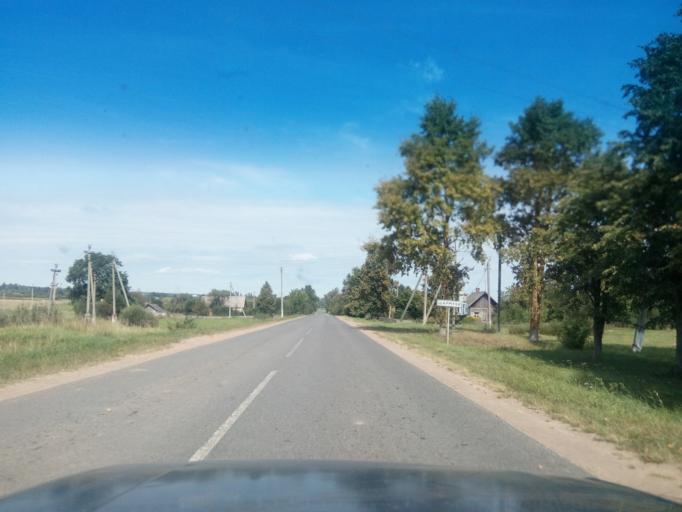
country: BY
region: Vitebsk
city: Vyerkhnyadzvinsk
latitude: 55.8232
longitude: 27.7348
